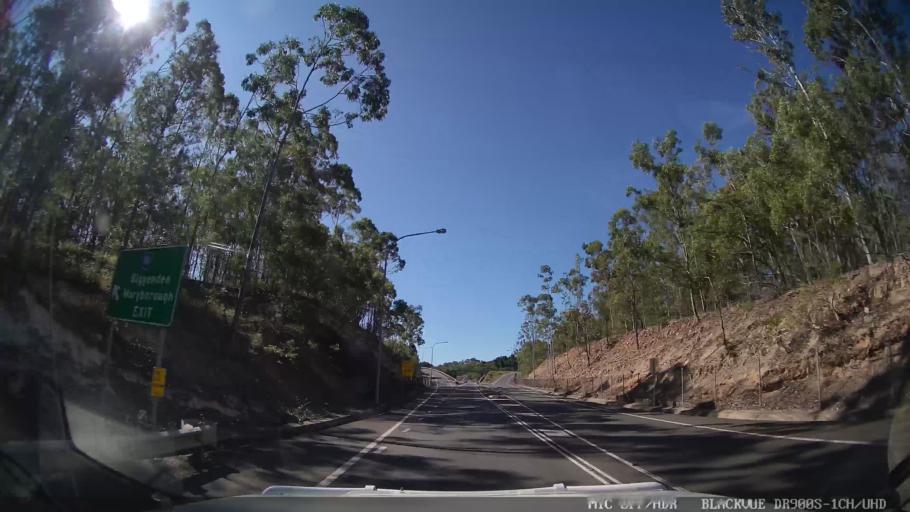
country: AU
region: Queensland
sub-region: Fraser Coast
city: Maryborough
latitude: -25.5218
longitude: 152.6671
